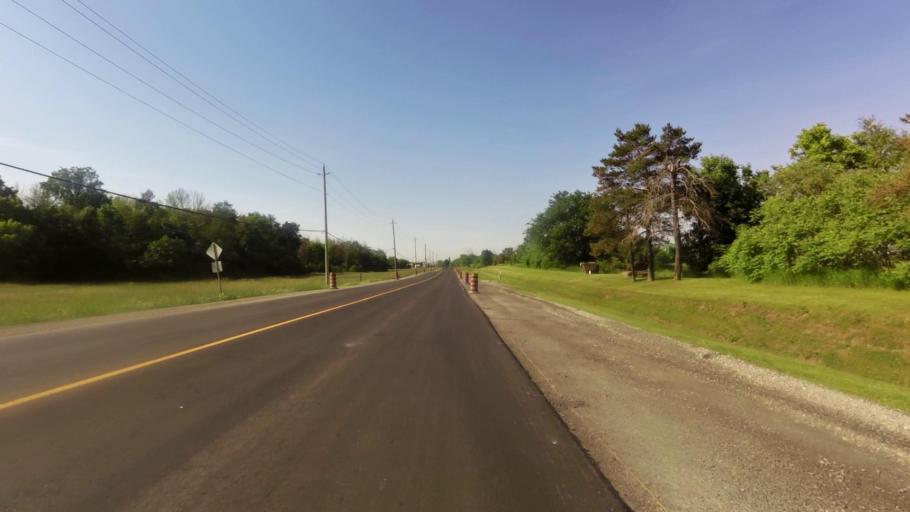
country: CA
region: Ontario
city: Ottawa
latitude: 45.2114
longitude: -75.5685
